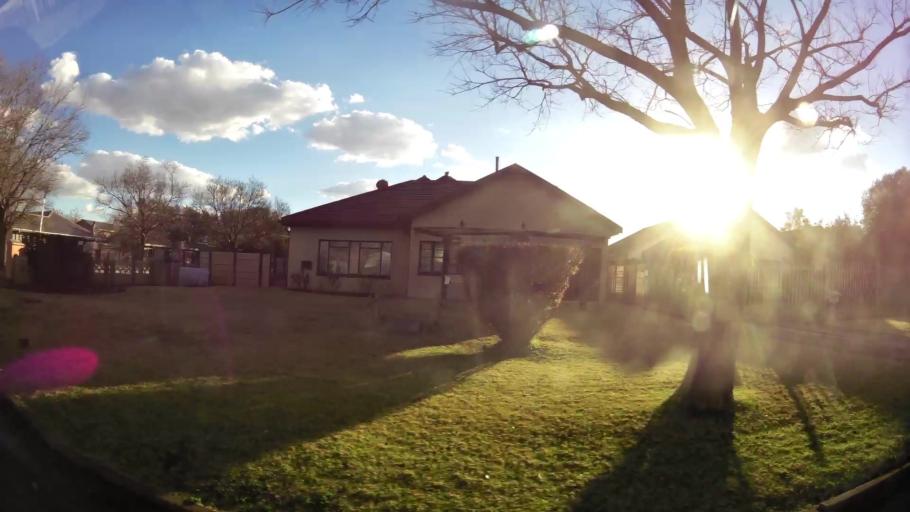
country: ZA
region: North-West
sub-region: Dr Kenneth Kaunda District Municipality
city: Potchefstroom
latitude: -26.7341
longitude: 27.0892
